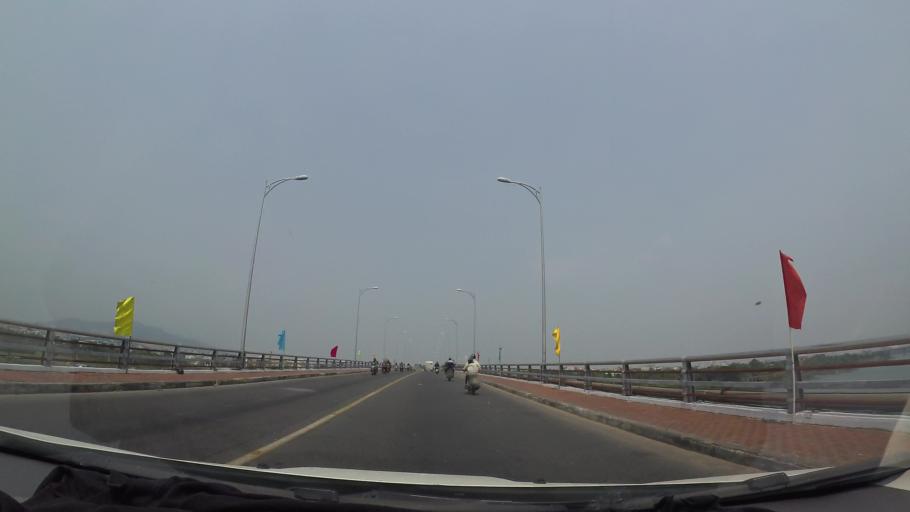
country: VN
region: Da Nang
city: Cam Le
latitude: 16.0078
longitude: 108.2073
